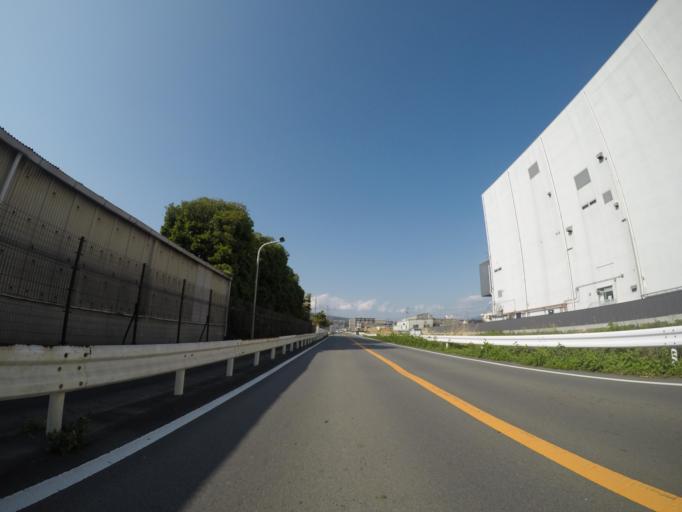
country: JP
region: Shizuoka
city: Numazu
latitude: 35.1133
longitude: 138.8490
